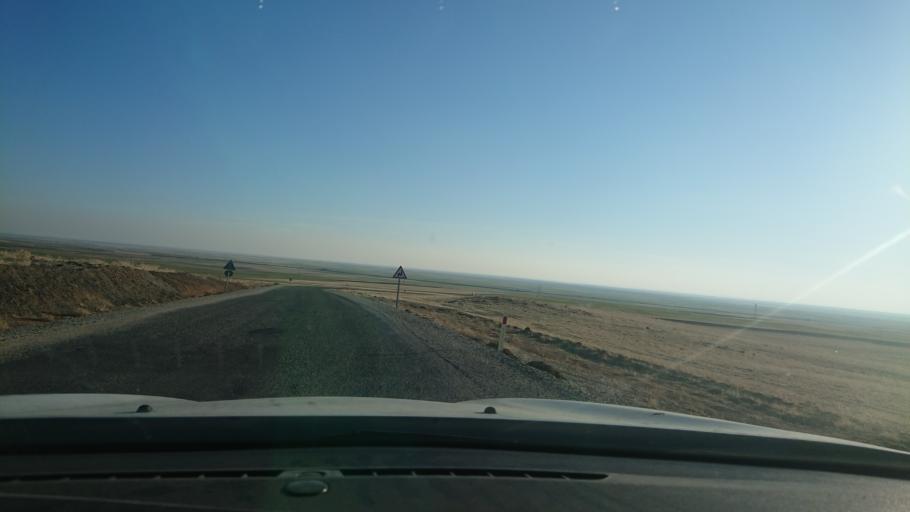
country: TR
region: Aksaray
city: Acipinar
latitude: 38.6816
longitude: 33.7341
